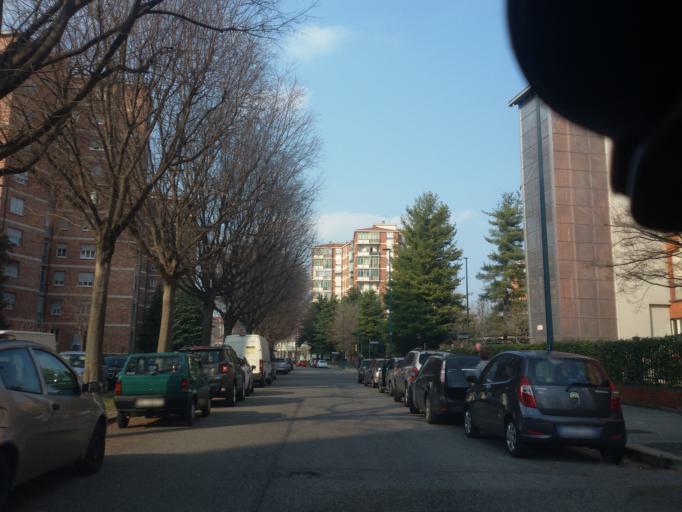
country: IT
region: Piedmont
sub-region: Provincia di Torino
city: Savonera
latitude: 45.1013
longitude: 7.6302
